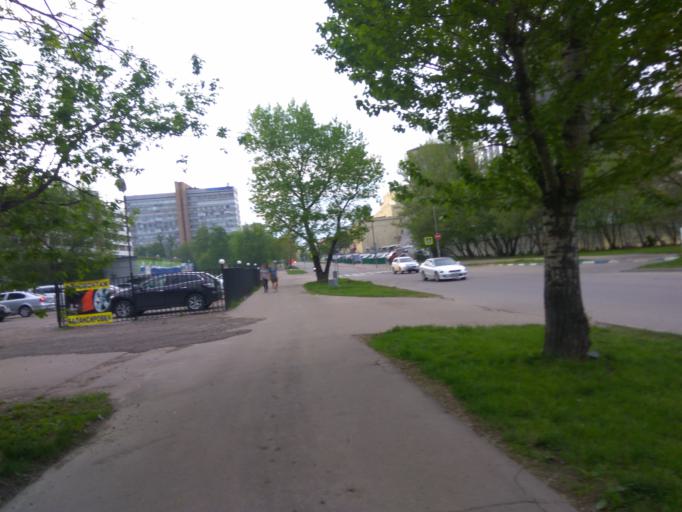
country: RU
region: Moscow
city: Sokol
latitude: 55.7790
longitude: 37.5015
